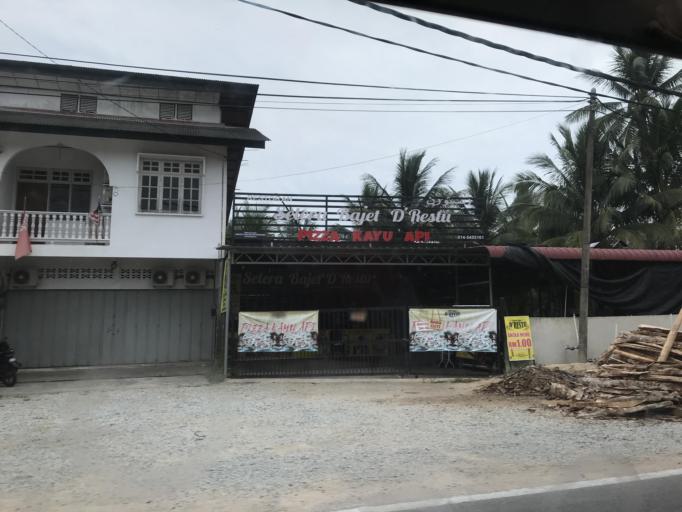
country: MY
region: Kelantan
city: Kota Bharu
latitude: 6.1594
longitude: 102.2270
